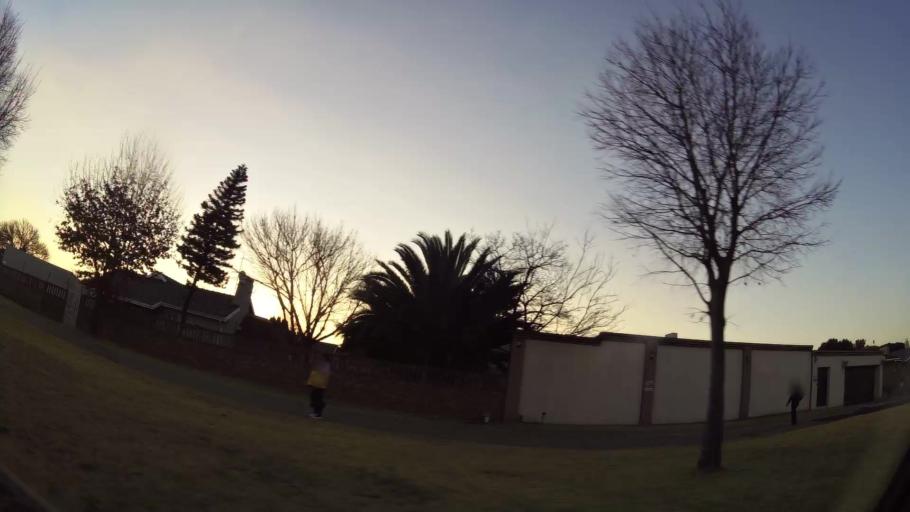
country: ZA
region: Gauteng
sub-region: Ekurhuleni Metropolitan Municipality
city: Germiston
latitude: -26.2685
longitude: 28.1564
